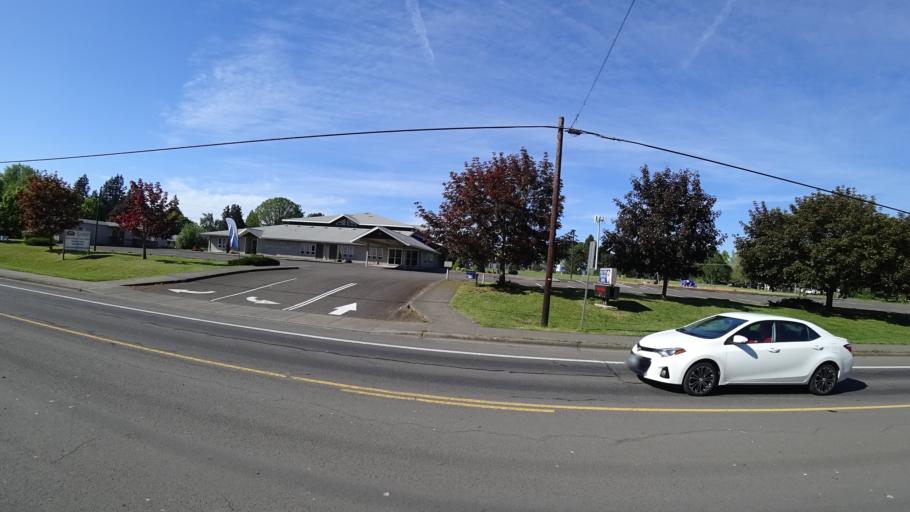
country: US
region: Oregon
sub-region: Washington County
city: Hillsboro
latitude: 45.5211
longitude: -122.9599
